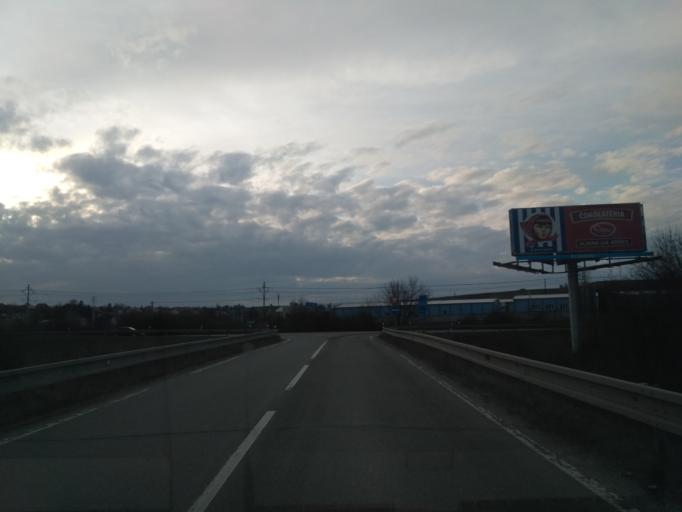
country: SK
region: Kosicky
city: Kosice
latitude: 48.6873
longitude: 21.2247
